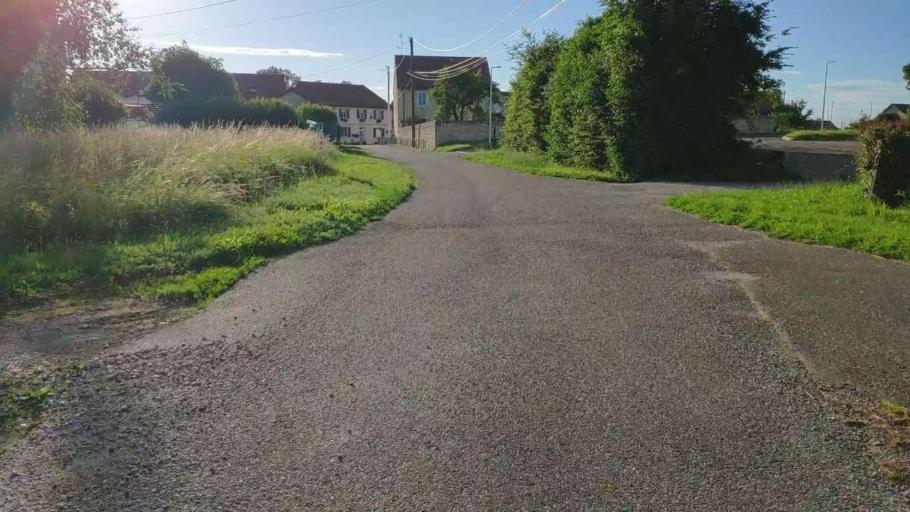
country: FR
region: Franche-Comte
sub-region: Departement du Jura
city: Bletterans
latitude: 46.7831
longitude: 5.5088
